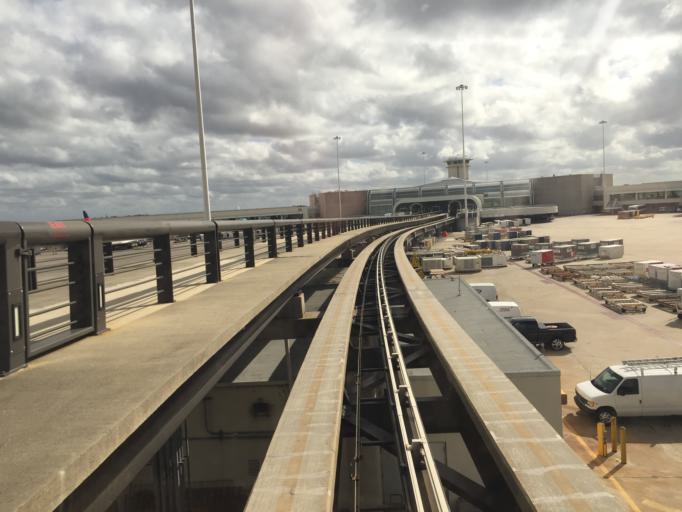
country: US
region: Florida
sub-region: Orange County
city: Taft
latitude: 28.4295
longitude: -81.3030
